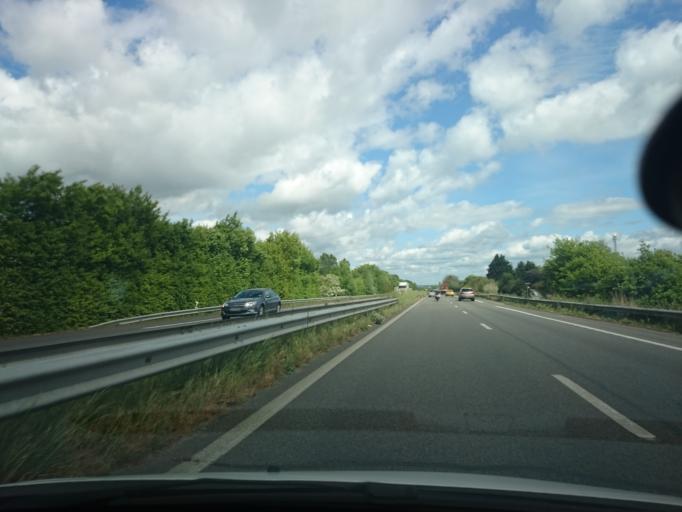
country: FR
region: Pays de la Loire
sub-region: Departement de la Loire-Atlantique
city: Donges
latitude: 47.3456
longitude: -2.0817
